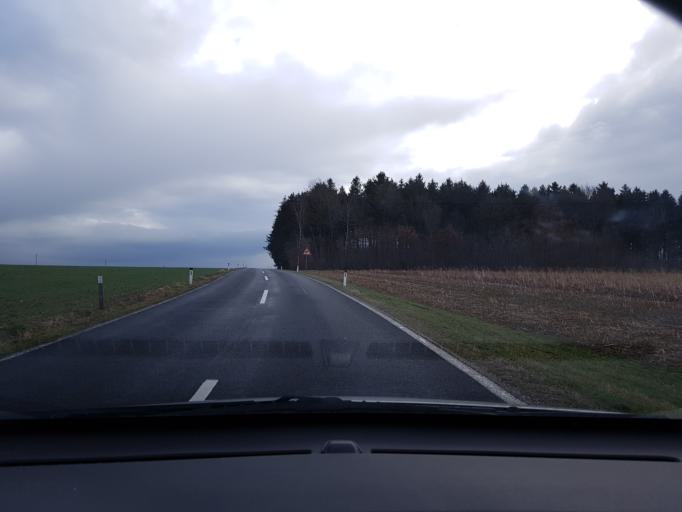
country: AT
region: Upper Austria
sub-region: Politischer Bezirk Linz-Land
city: Sankt Florian
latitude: 48.1521
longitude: 14.3621
